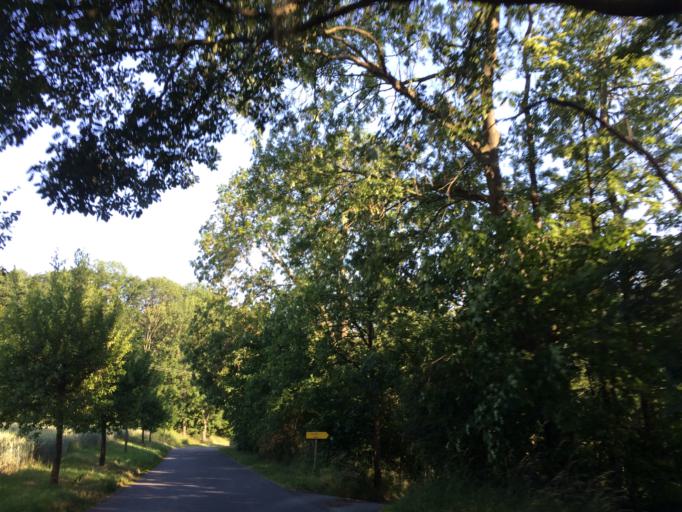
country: DE
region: Thuringia
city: Gossitz
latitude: 50.6099
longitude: 11.5960
